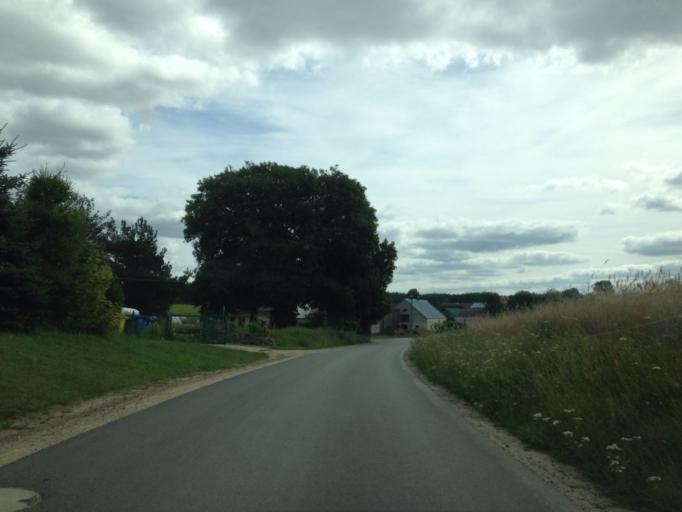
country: PL
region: Pomeranian Voivodeship
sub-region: Powiat koscierski
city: Lipusz
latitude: 54.0741
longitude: 17.7225
